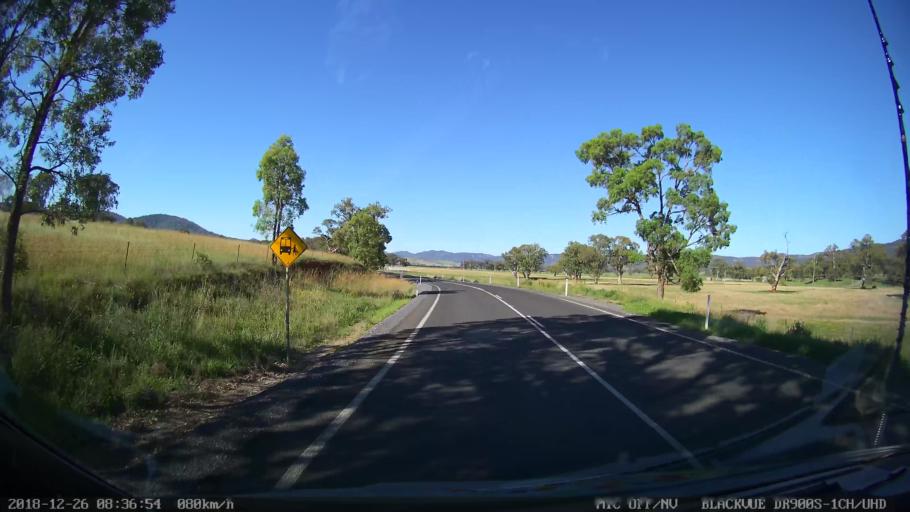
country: AU
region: New South Wales
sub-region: Upper Hunter Shire
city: Merriwa
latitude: -32.4268
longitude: 150.0948
